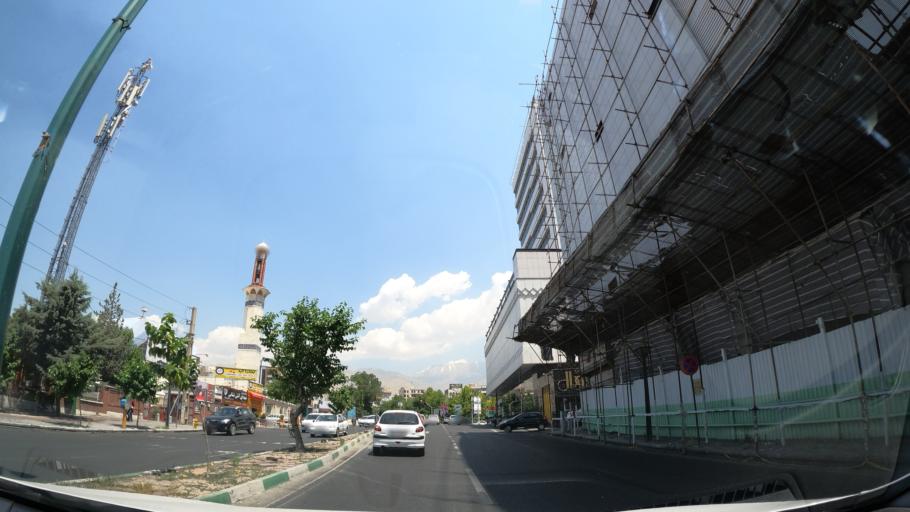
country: IR
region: Tehran
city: Tajrish
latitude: 35.7699
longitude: 51.3789
